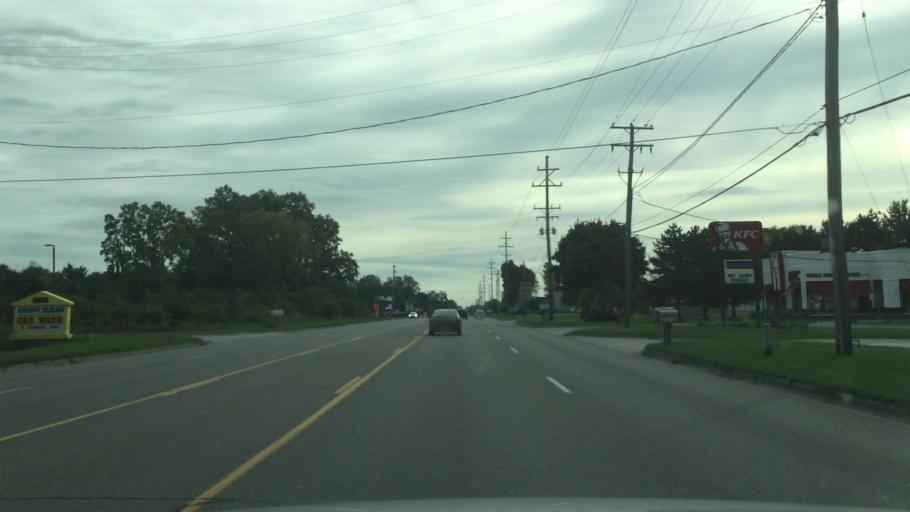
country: US
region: Michigan
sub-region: Genesee County
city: Flint
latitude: 42.9738
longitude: -83.7104
